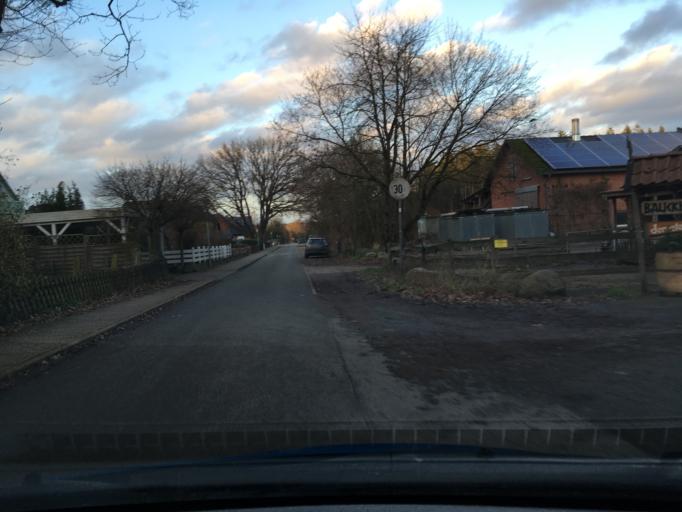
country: DE
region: Lower Saxony
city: Amelinghausen
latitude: 53.1339
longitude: 10.2189
